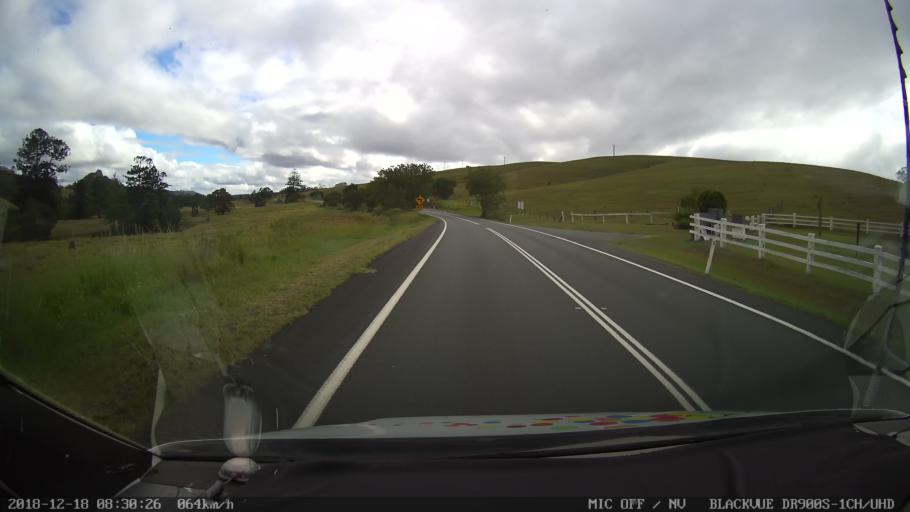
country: AU
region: New South Wales
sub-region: Kyogle
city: Kyogle
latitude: -28.3221
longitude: 152.7694
